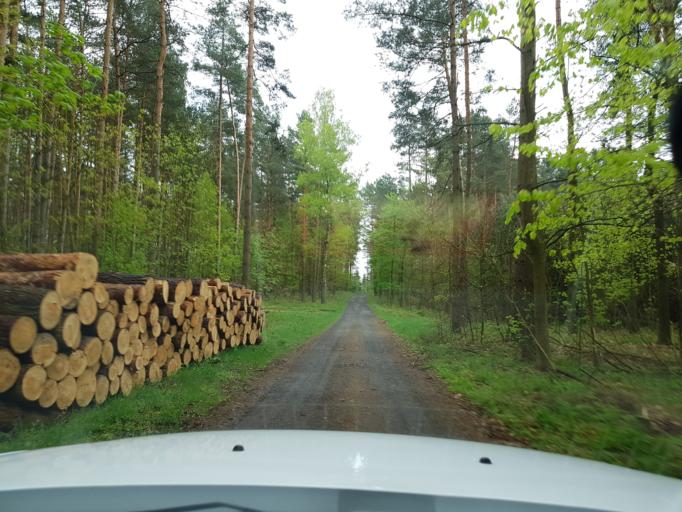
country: PL
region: West Pomeranian Voivodeship
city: Trzcinsko Zdroj
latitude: 52.9915
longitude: 14.6729
